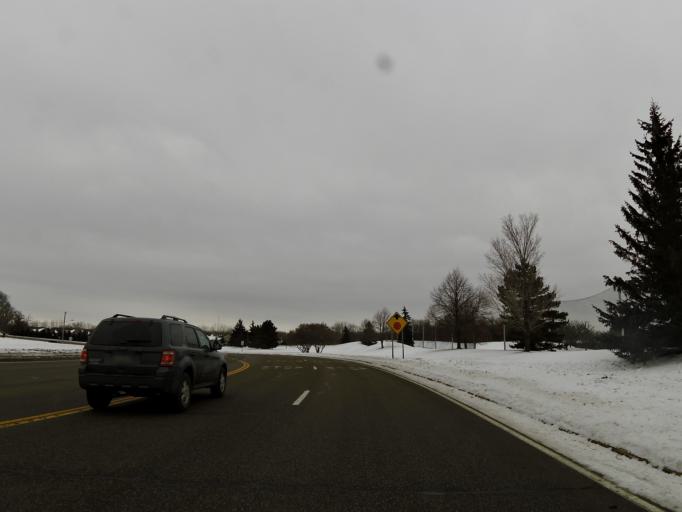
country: US
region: Minnesota
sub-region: Dakota County
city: Inver Grove Heights
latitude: 44.8470
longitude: -93.0681
